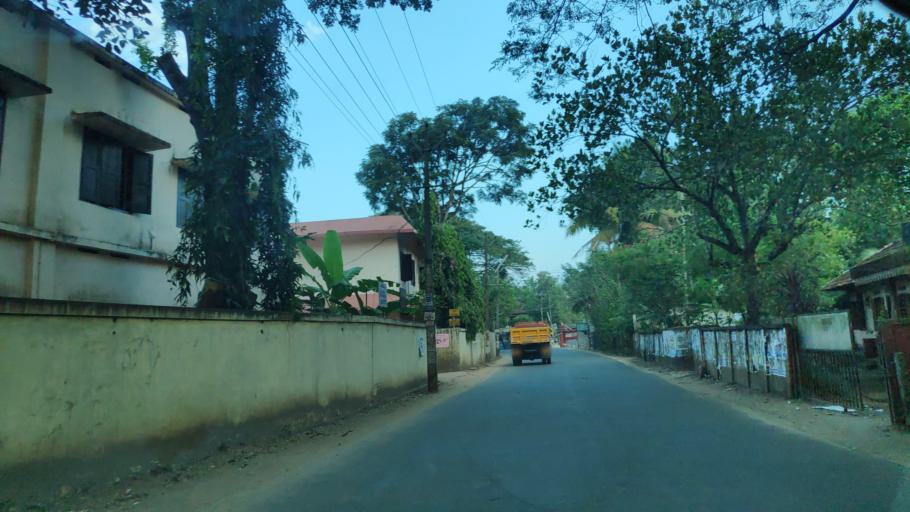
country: IN
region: Kerala
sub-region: Alappuzha
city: Shertallai
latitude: 9.6642
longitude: 76.3834
